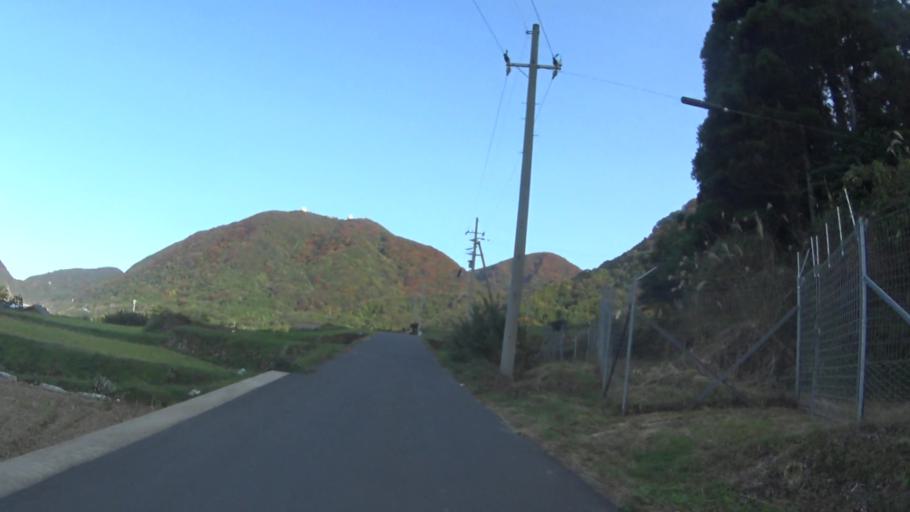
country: JP
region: Kyoto
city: Miyazu
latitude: 35.7623
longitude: 135.2010
